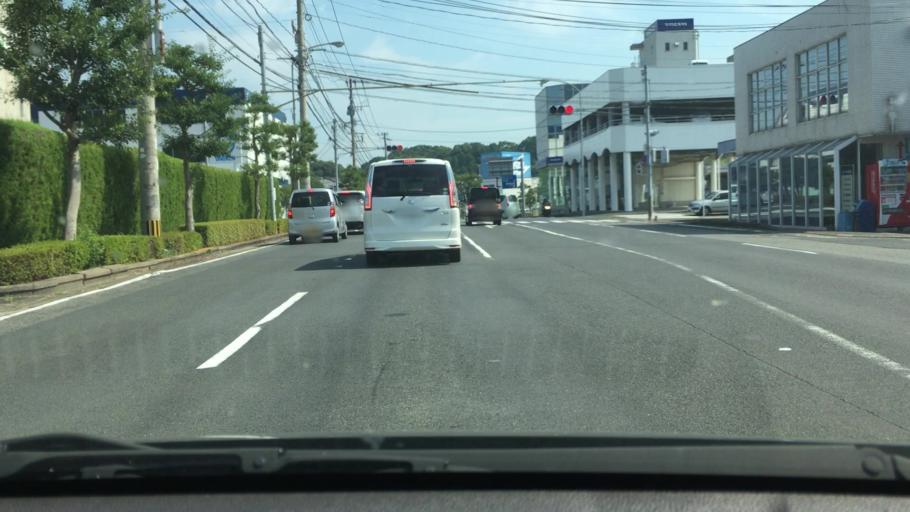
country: JP
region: Nagasaki
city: Sasebo
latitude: 33.1506
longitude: 129.7711
